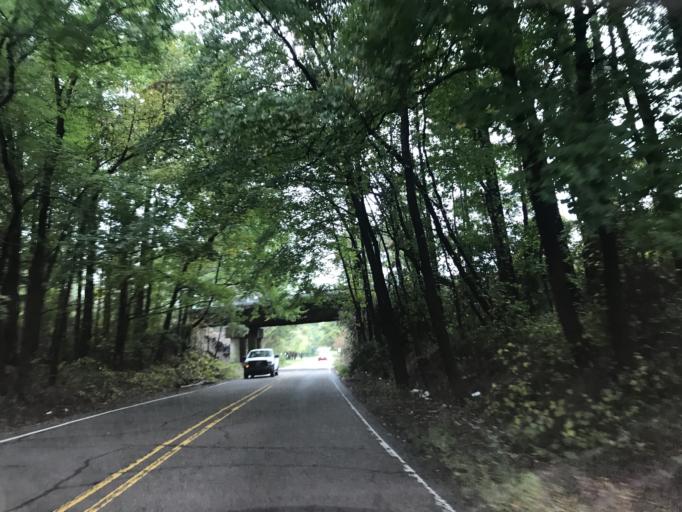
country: US
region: North Carolina
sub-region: Wake County
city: Cary
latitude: 35.7900
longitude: -78.7743
